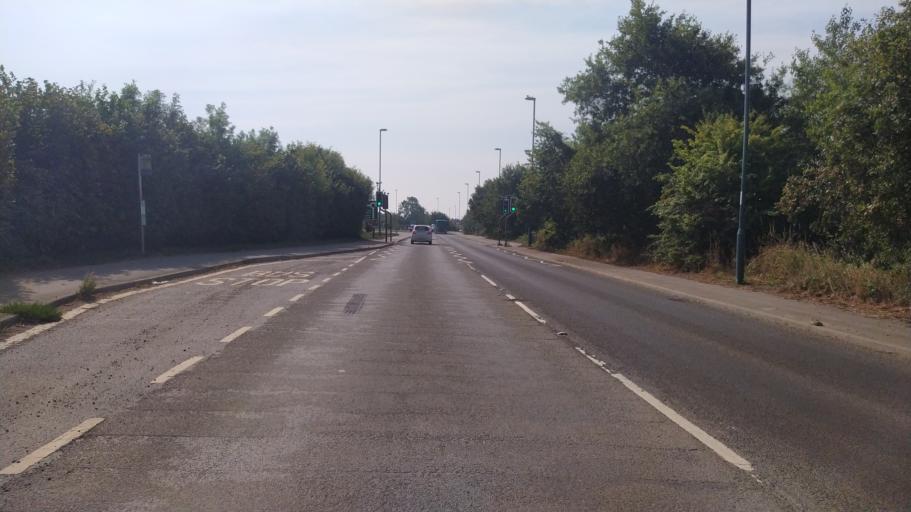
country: GB
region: England
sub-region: West Sussex
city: Bognor Regis
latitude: 50.8070
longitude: -0.7015
